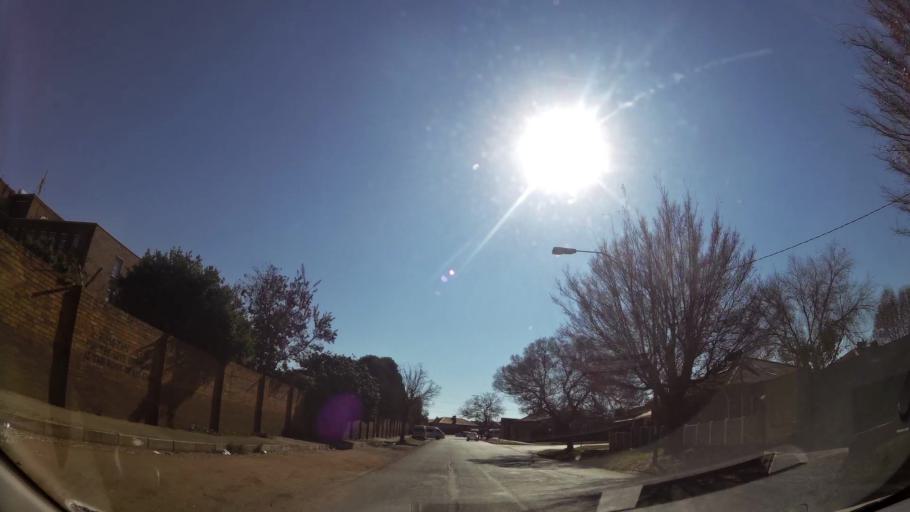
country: ZA
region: Gauteng
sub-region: City of Johannesburg Metropolitan Municipality
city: Johannesburg
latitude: -26.1892
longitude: 27.9737
